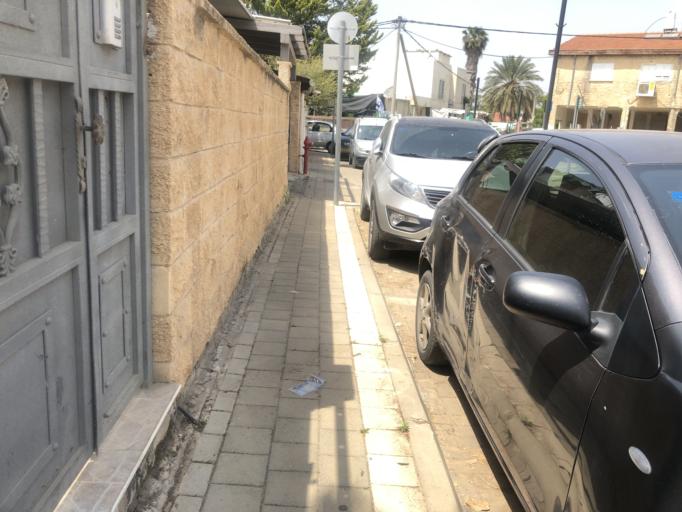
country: IL
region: Central District
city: Rosh Ha'Ayin
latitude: 32.1020
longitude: 34.9395
